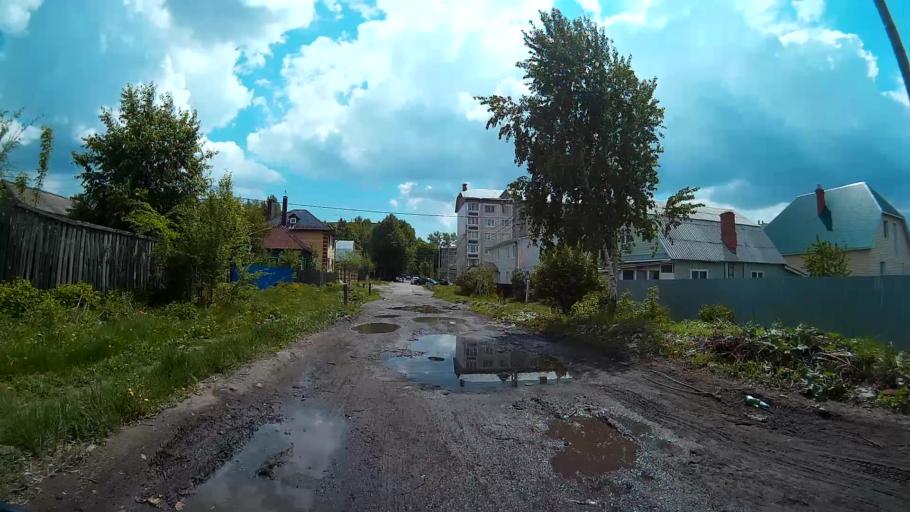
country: RU
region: Ulyanovsk
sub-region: Ulyanovskiy Rayon
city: Ulyanovsk
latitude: 54.3429
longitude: 48.3677
